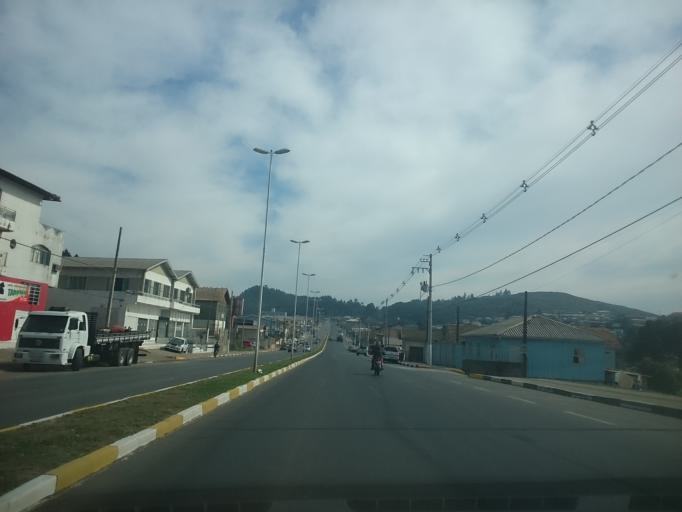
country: BR
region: Santa Catarina
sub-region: Lages
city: Lages
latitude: -27.8301
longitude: -50.3417
